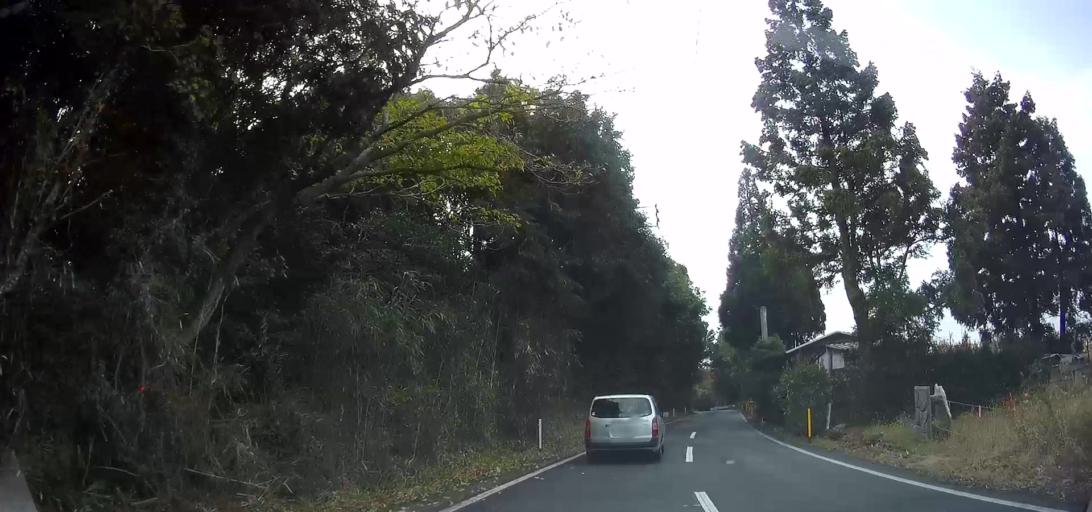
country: JP
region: Nagasaki
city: Shimabara
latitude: 32.7003
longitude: 130.2480
